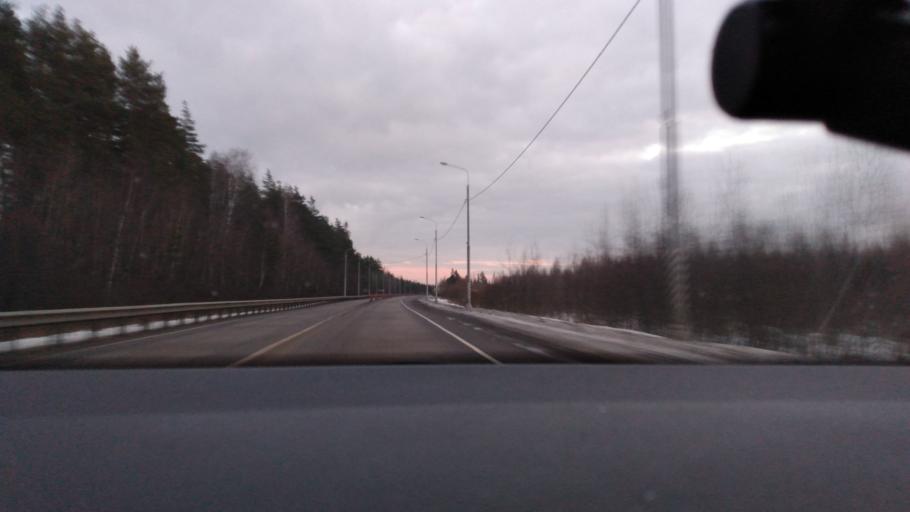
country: RU
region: Moskovskaya
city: Yegor'yevsk
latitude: 55.4496
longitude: 39.0065
